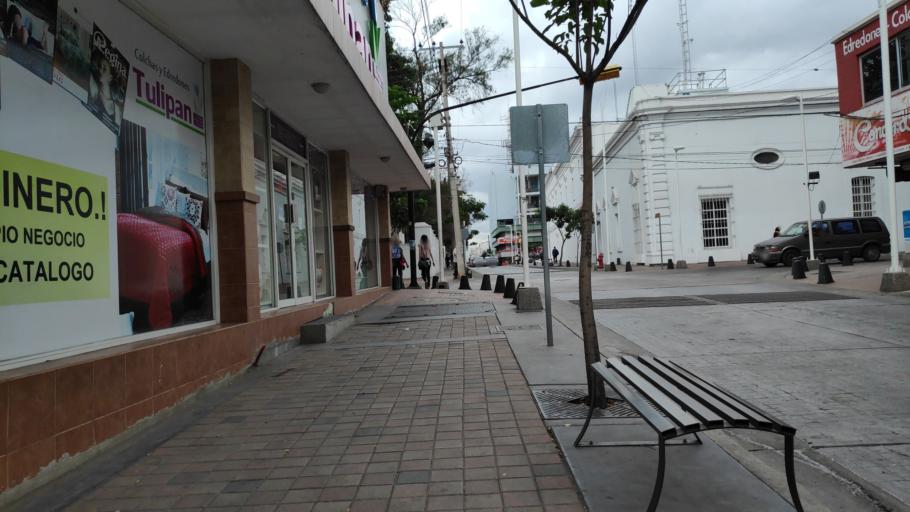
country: MX
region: Sinaloa
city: Culiacan
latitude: 24.8067
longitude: -107.3930
